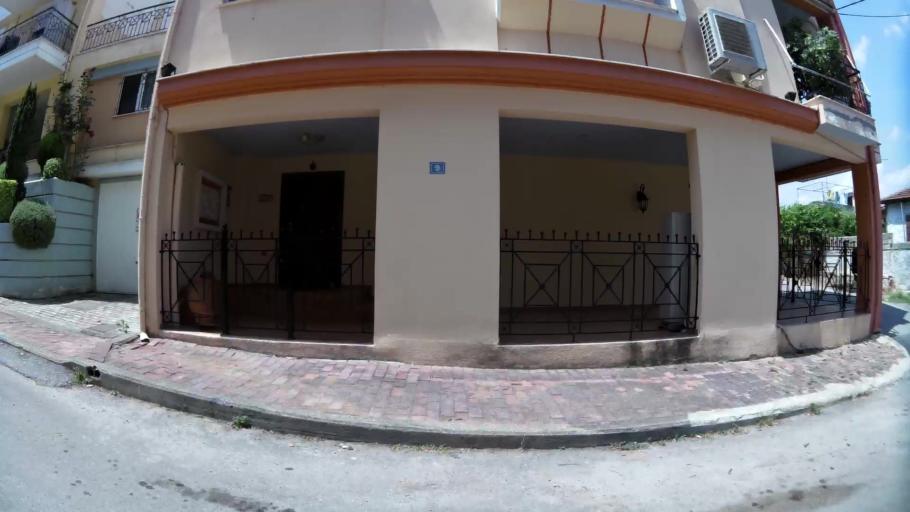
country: GR
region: Central Macedonia
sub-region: Nomos Imathias
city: Veroia
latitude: 40.5186
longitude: 22.1968
